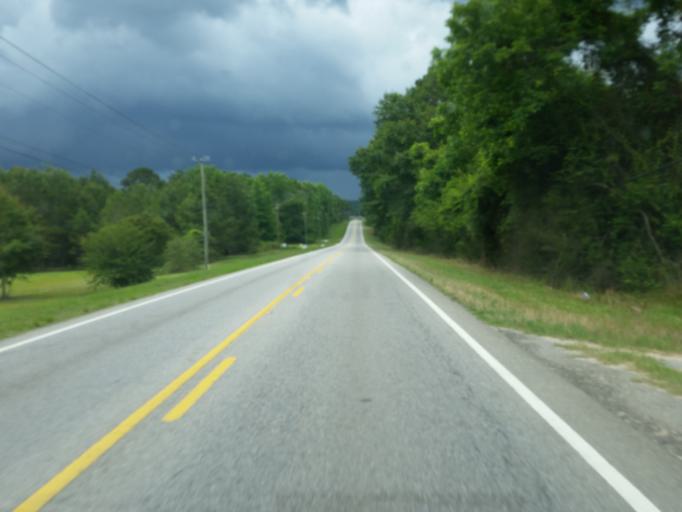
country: US
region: Mississippi
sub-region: Jackson County
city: Hurley
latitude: 30.8095
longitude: -88.3410
